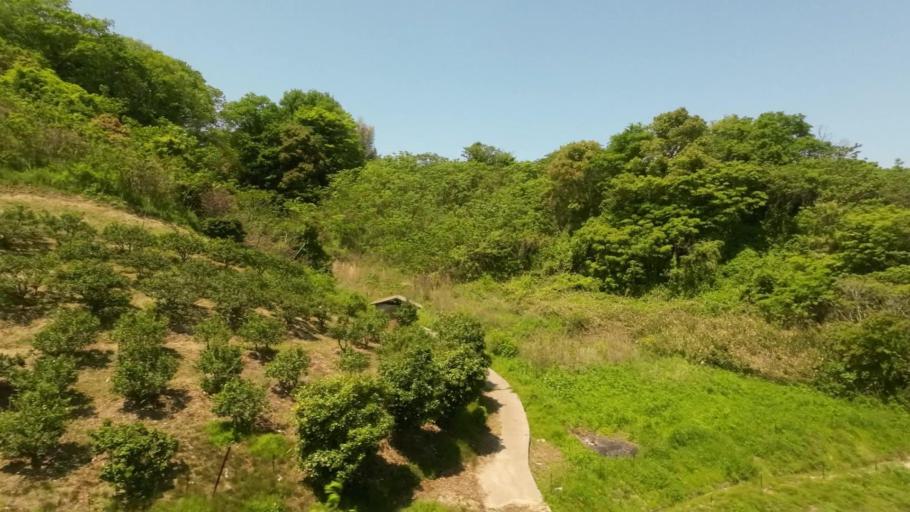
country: JP
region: Ehime
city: Hojo
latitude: 33.9981
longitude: 132.7751
